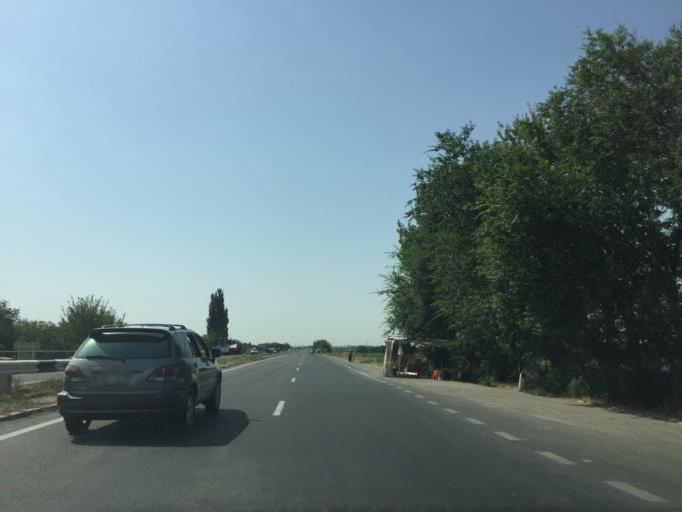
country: AM
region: Ararat
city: Aralez
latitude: 39.9070
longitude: 44.6077
